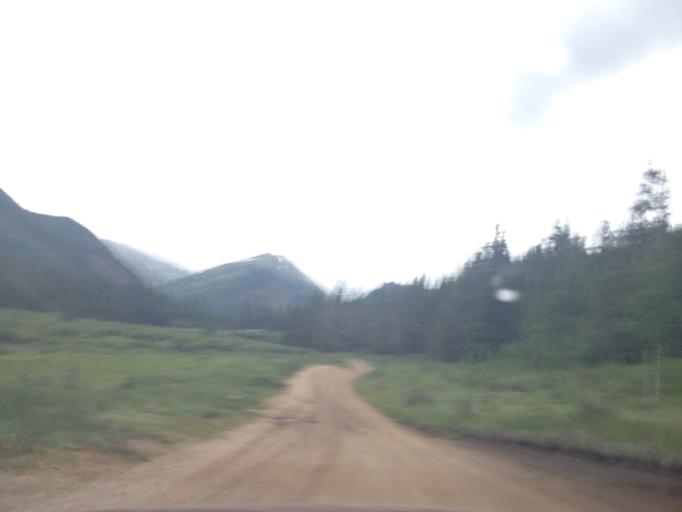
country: US
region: Colorado
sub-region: Clear Creek County
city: Georgetown
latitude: 39.5458
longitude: -105.7476
